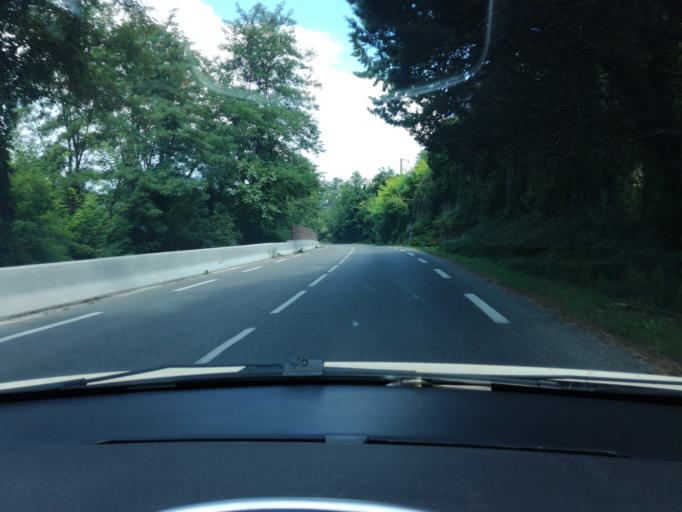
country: FR
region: Rhone-Alpes
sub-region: Departement de l'Ardeche
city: Ruoms
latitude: 44.4801
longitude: 4.3791
